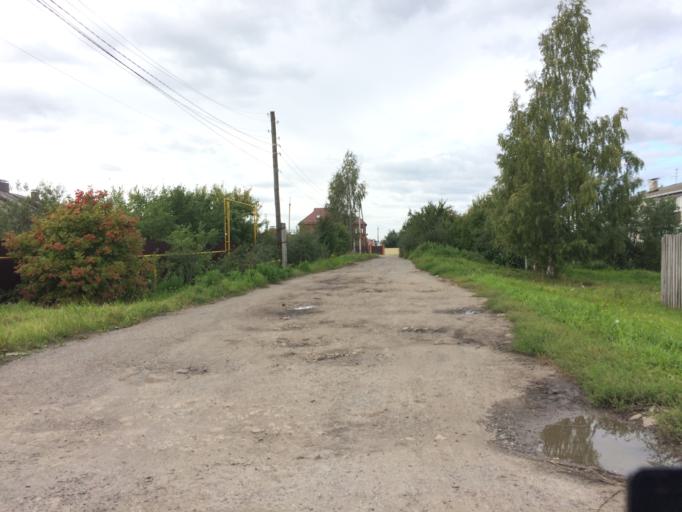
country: RU
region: Mariy-El
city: Yoshkar-Ola
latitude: 56.6621
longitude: 47.9930
